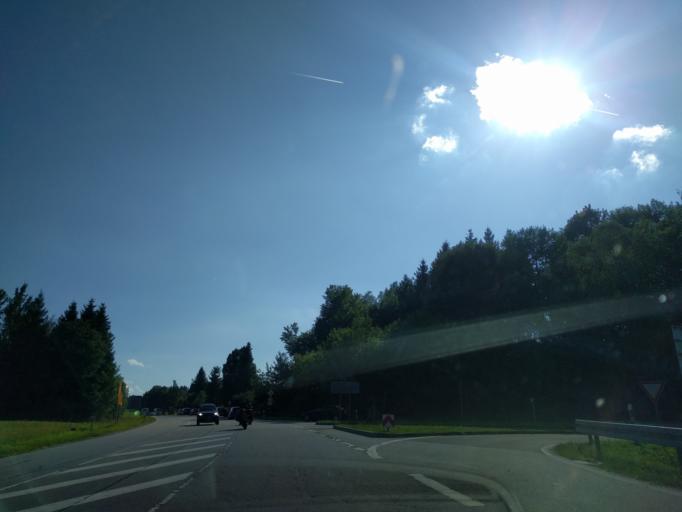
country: DE
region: Bavaria
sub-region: Lower Bavaria
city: Bischofsmais
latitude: 48.9054
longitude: 13.0988
